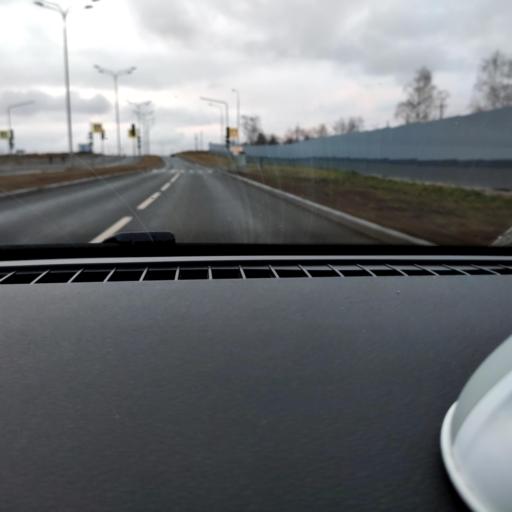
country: RU
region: Samara
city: Samara
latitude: 53.2856
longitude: 50.2350
